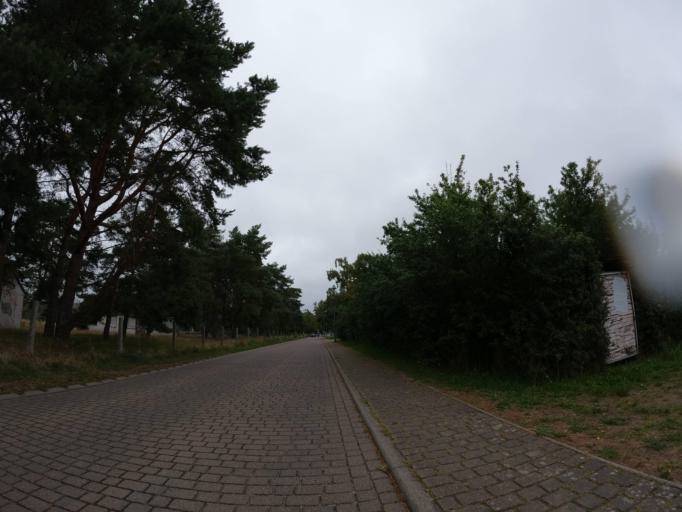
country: DE
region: Mecklenburg-Vorpommern
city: Ostseebad Gohren
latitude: 54.3331
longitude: 13.7330
